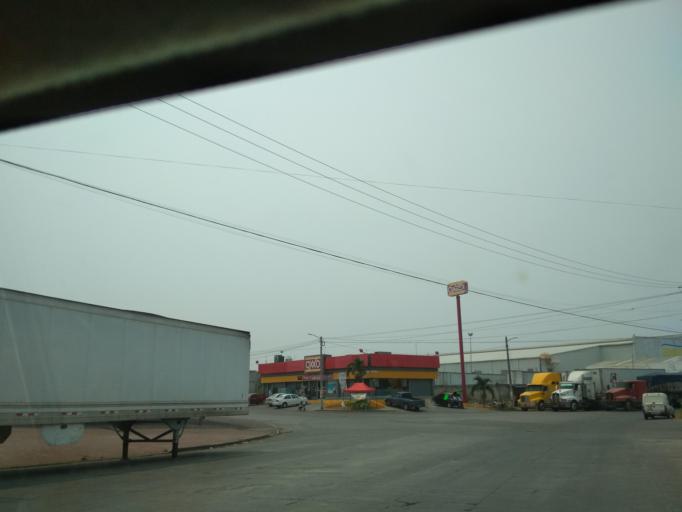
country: MX
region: Veracruz
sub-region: Veracruz
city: Las Amapolas
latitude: 19.1634
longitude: -96.2263
